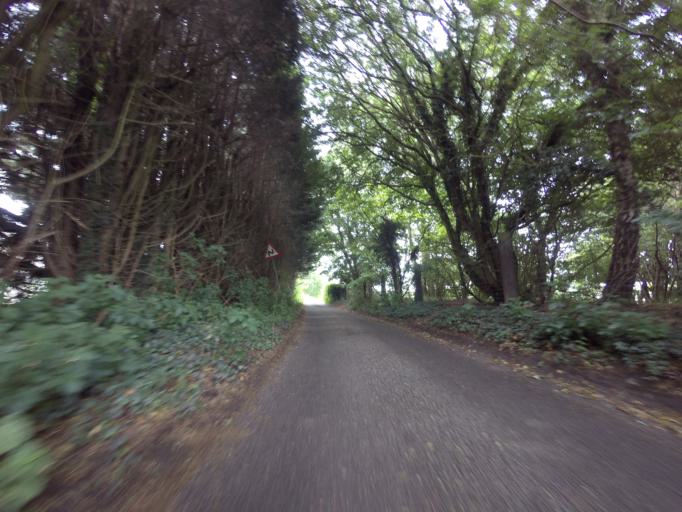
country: GB
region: England
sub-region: Greater London
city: Orpington
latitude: 51.3721
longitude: 0.1368
